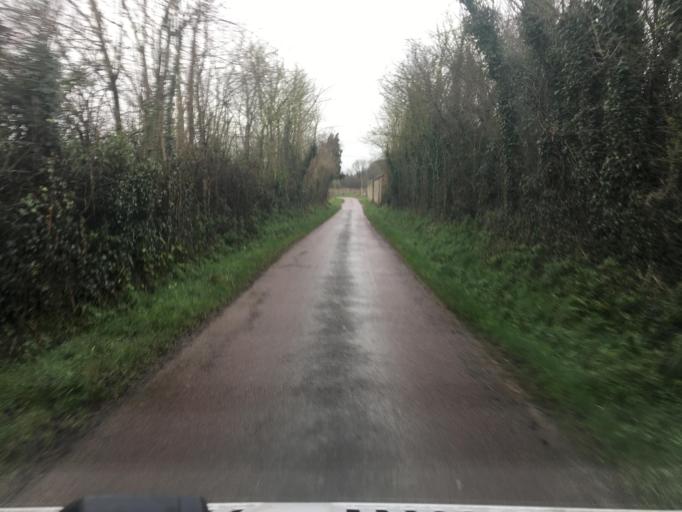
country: FR
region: Lower Normandy
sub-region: Departement de la Manche
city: Sainte-Mere-Eglise
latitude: 49.4248
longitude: -1.2663
